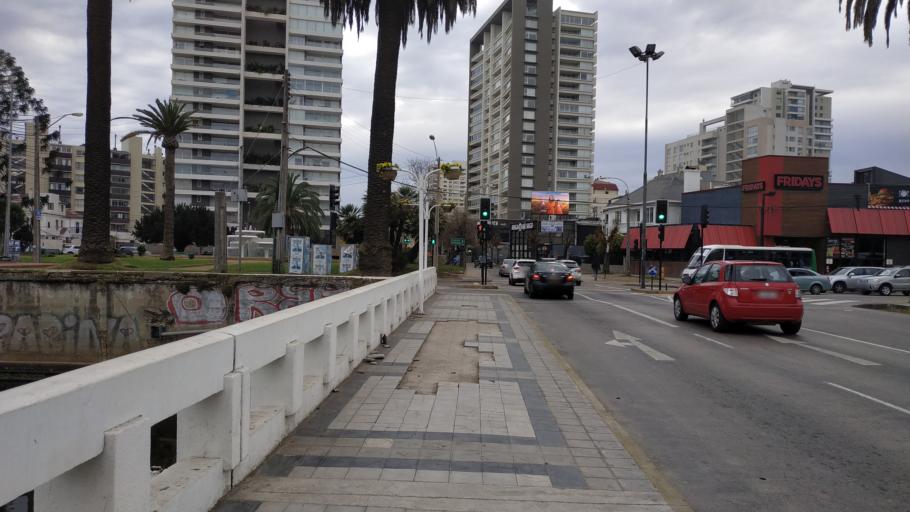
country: CL
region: Valparaiso
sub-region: Provincia de Valparaiso
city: Vina del Mar
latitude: -33.0213
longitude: -71.5592
